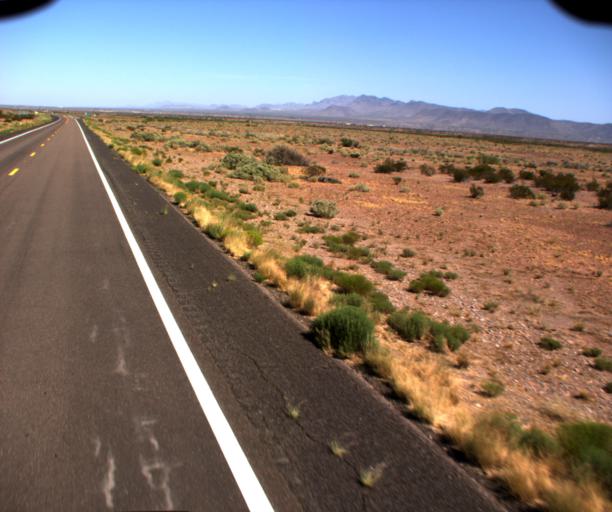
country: US
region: Arizona
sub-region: Graham County
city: Safford
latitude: 32.7887
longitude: -109.5461
